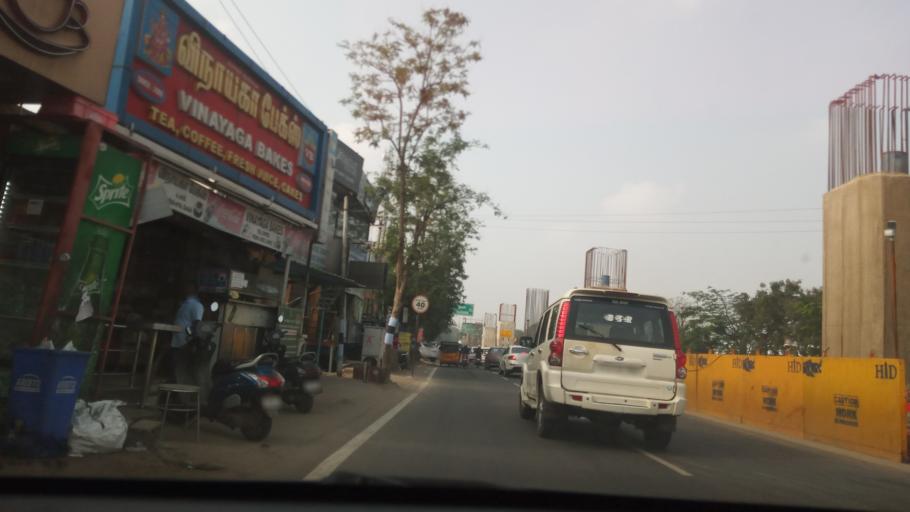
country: IN
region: Tamil Nadu
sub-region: Coimbatore
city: Irugur
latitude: 11.0364
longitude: 77.0356
